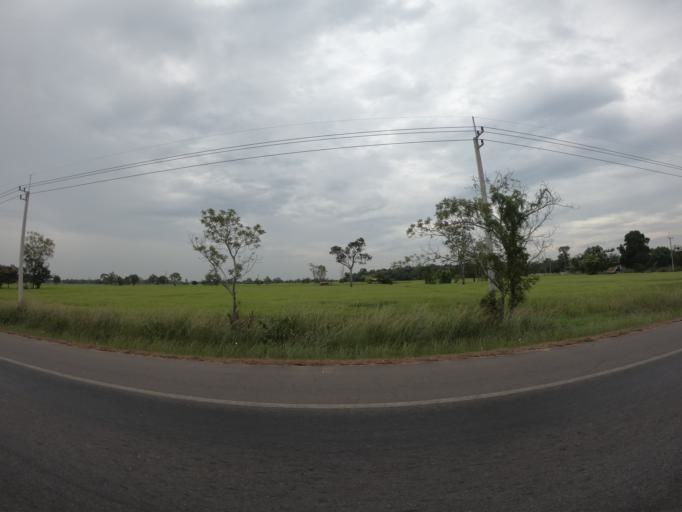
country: TH
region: Roi Et
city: Chiang Khwan
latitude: 16.1053
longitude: 103.8186
